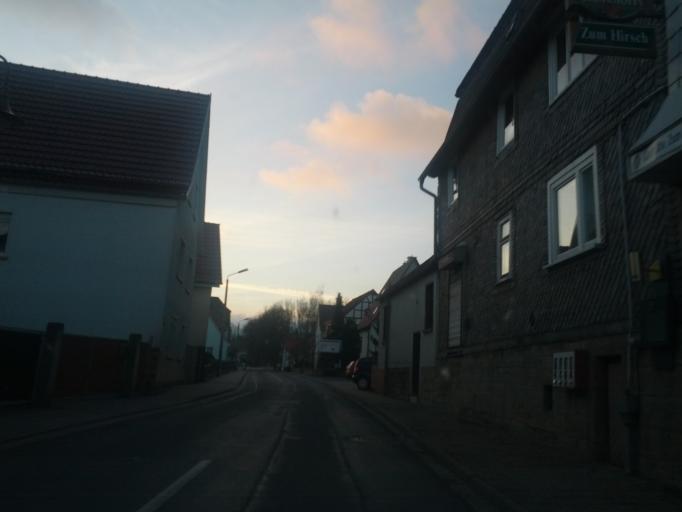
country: DE
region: Thuringia
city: Katharinenberg
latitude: 51.1761
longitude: 10.2800
